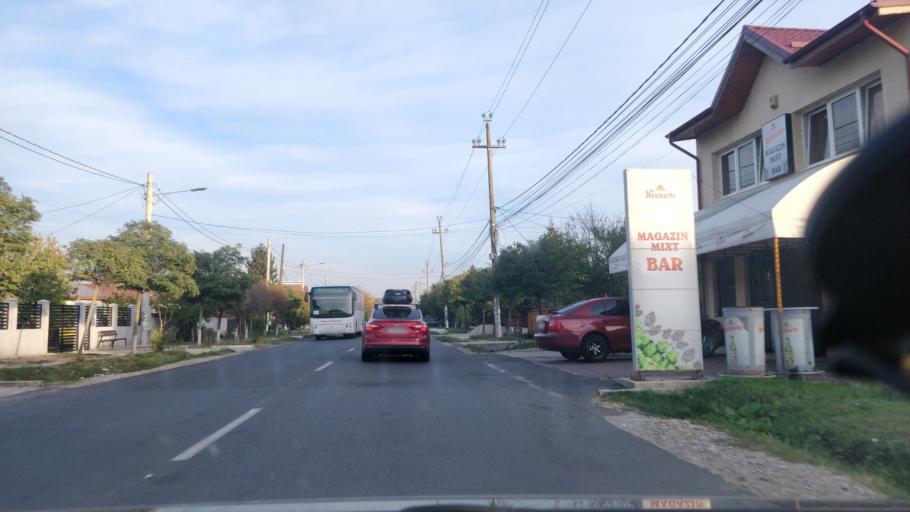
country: RO
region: Ilfov
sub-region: Comuna Ciorogarla
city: Ciorogarla
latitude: 44.4439
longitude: 25.8692
